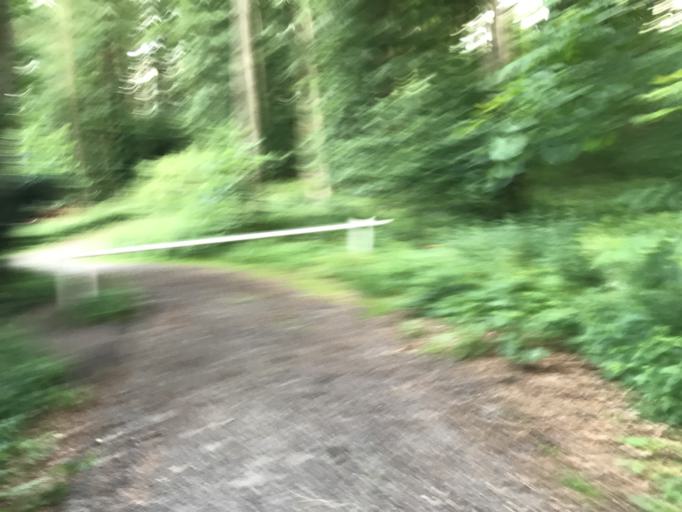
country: DE
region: Hesse
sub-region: Regierungsbezirk Giessen
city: Lich
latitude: 50.5095
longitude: 8.8186
